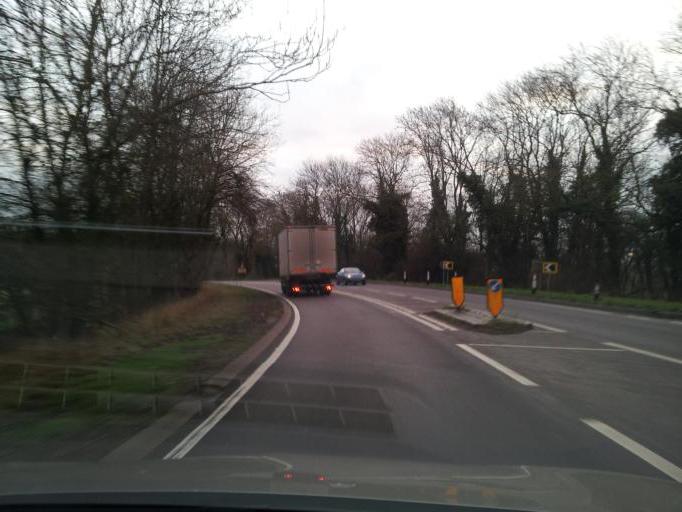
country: GB
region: England
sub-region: Cambridgeshire
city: Girton
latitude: 52.2145
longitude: 0.0630
